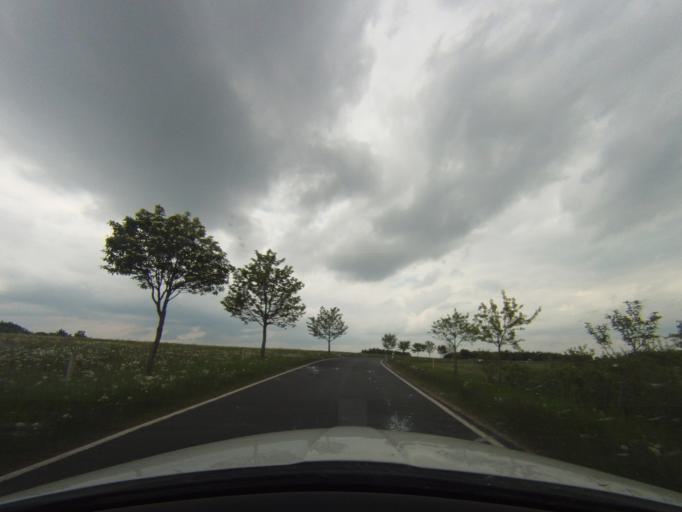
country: DE
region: Thuringia
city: Drobischau
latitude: 50.6332
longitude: 11.0739
